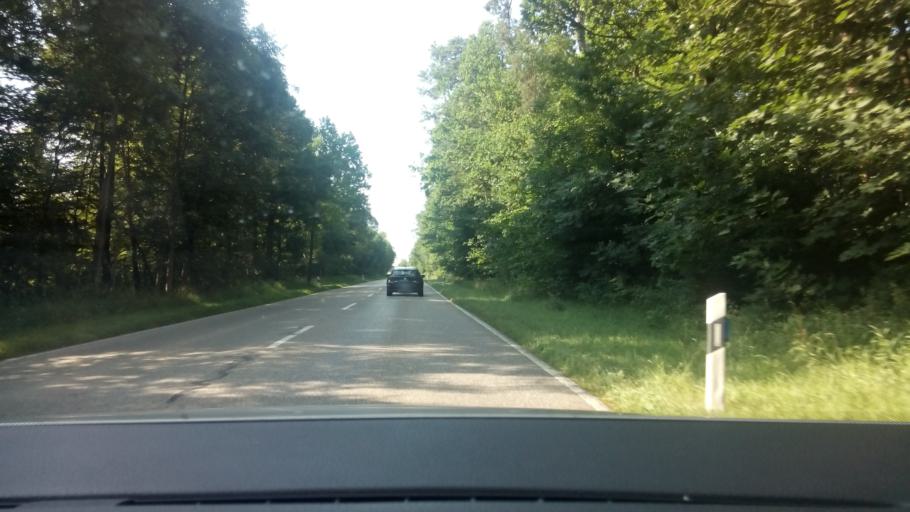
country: DE
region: Bavaria
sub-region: Upper Bavaria
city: Oberschleissheim
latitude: 48.2369
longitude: 11.5831
